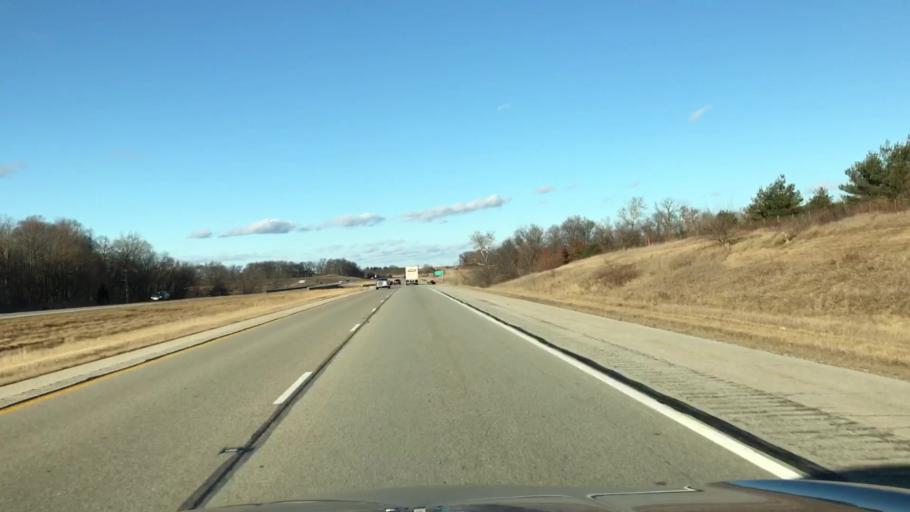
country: US
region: Illinois
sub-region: McLean County
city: Lexington
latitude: 40.6275
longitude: -88.8167
